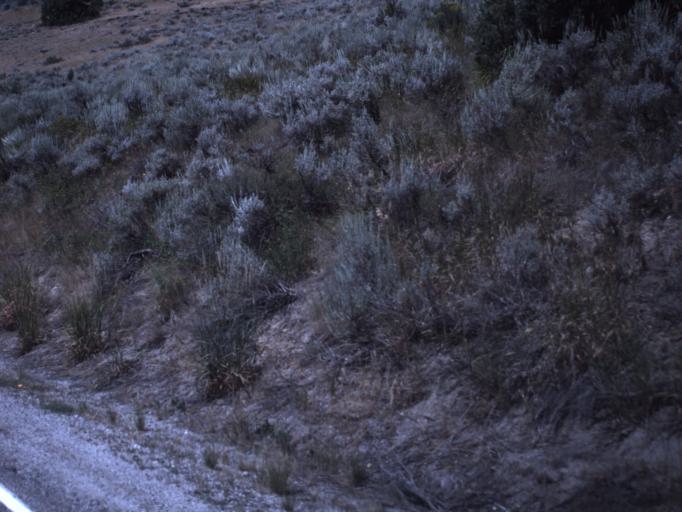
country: US
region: Utah
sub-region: Cache County
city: North Logan
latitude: 41.8330
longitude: -111.5956
